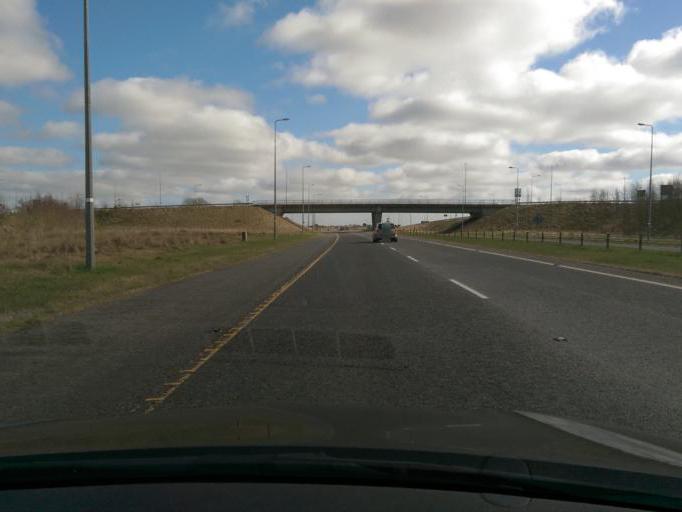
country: IE
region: Leinster
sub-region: An Iarmhi
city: Kinnegad
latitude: 53.4490
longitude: -7.1261
